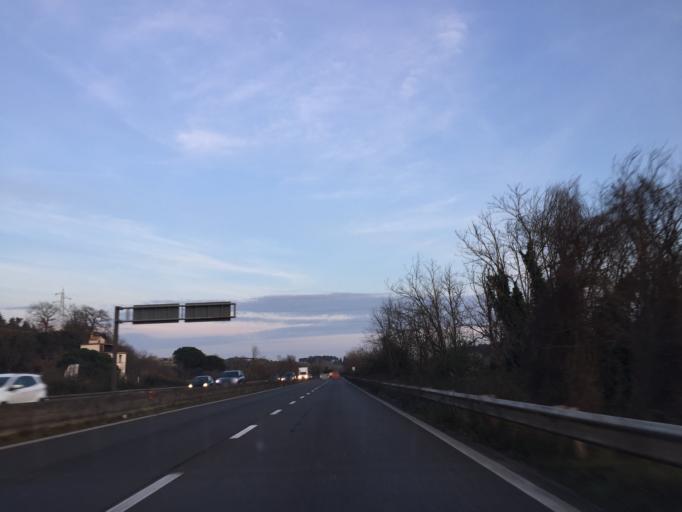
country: IT
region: Latium
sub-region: Citta metropolitana di Roma Capitale
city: Monte Caminetto
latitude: 41.9976
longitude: 12.4574
